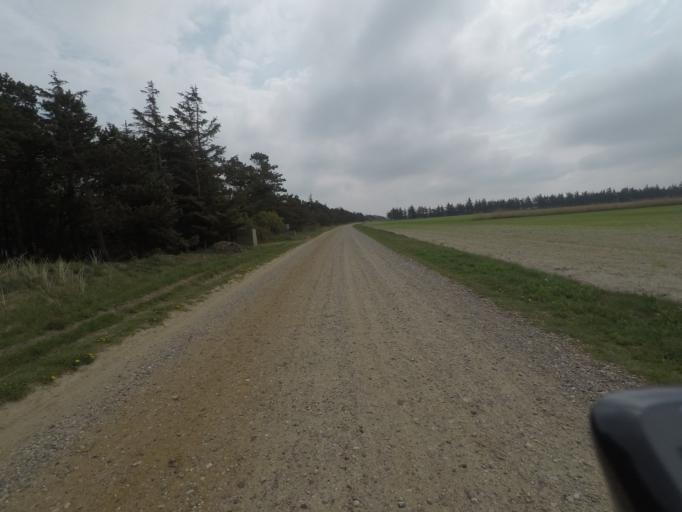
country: DE
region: Schleswig-Holstein
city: List
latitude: 55.0925
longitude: 8.5198
